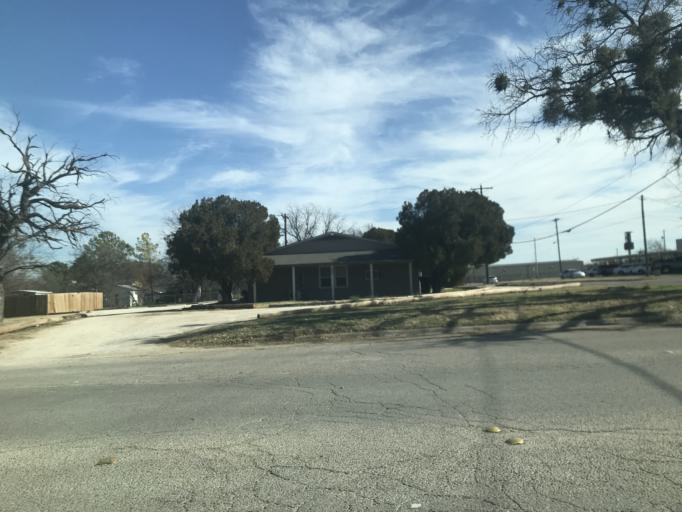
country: US
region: Texas
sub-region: Taylor County
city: Abilene
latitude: 32.4205
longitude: -99.7494
